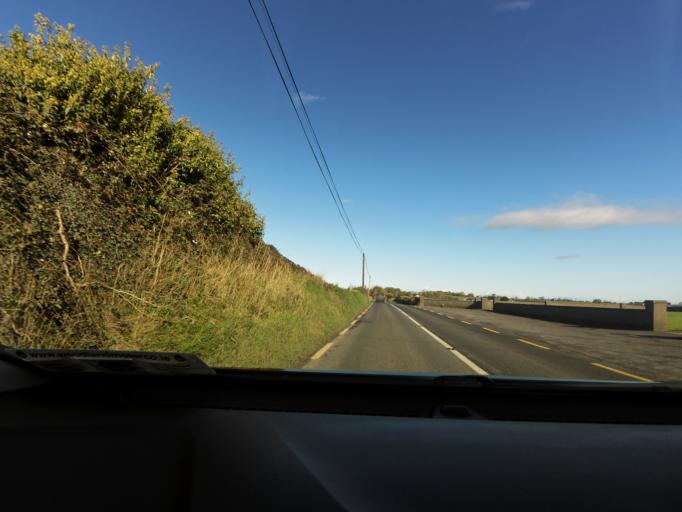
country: IE
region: Connaught
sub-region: County Galway
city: Moycullen
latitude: 53.4928
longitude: -9.0805
